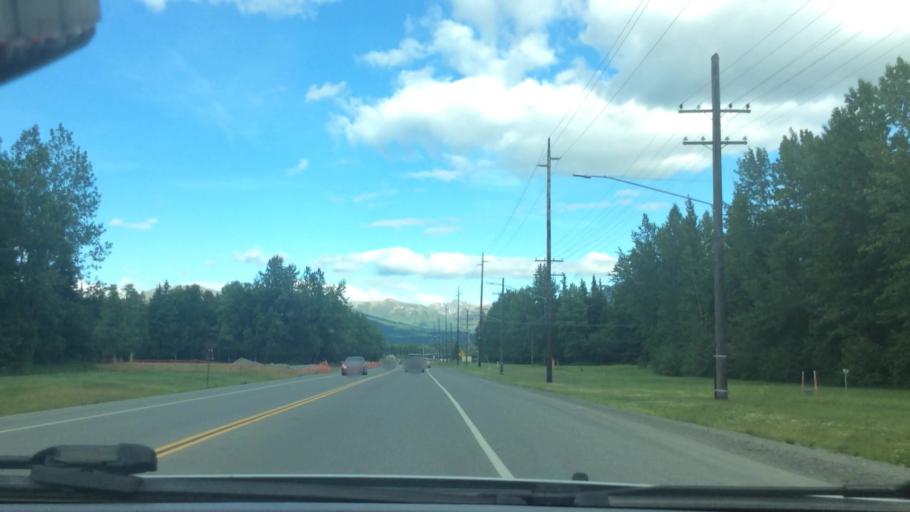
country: US
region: Alaska
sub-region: Anchorage Municipality
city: Elmendorf Air Force Base
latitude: 61.2314
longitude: -149.7587
